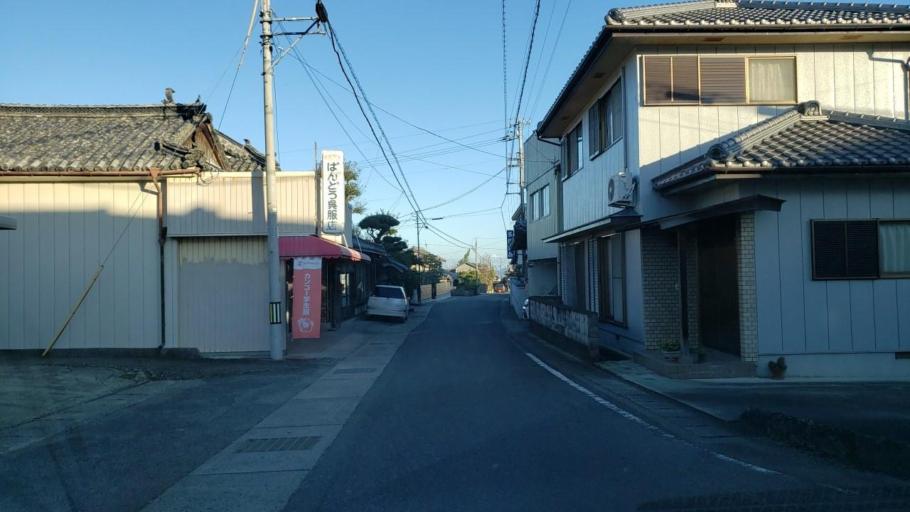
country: JP
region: Tokushima
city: Wakimachi
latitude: 34.0918
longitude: 134.2440
